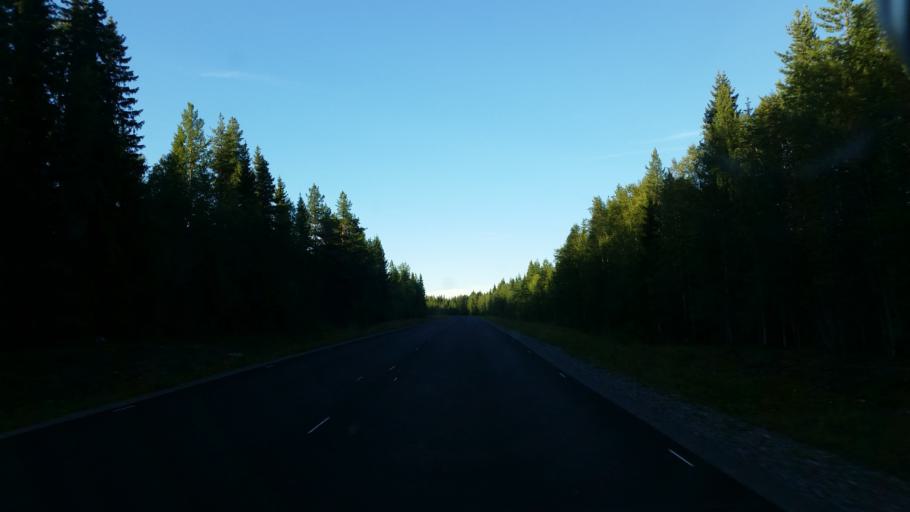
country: SE
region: Vaesterbotten
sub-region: Dorotea Kommun
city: Dorotea
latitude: 64.3076
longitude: 16.5982
